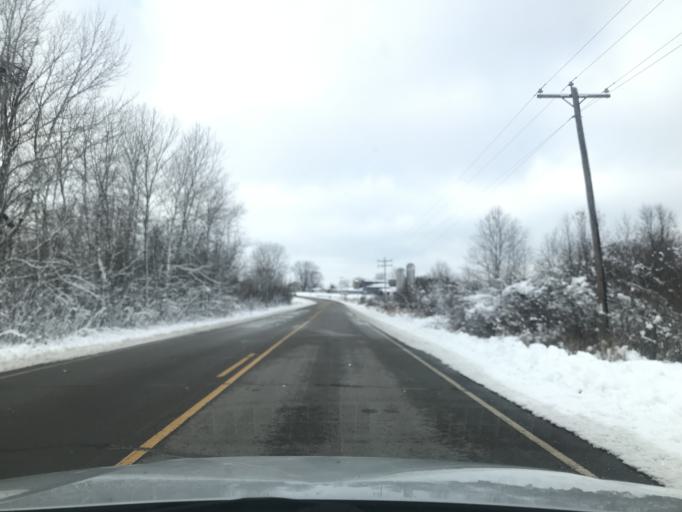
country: US
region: Wisconsin
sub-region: Oconto County
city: Oconto
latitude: 44.9494
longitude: -87.8818
